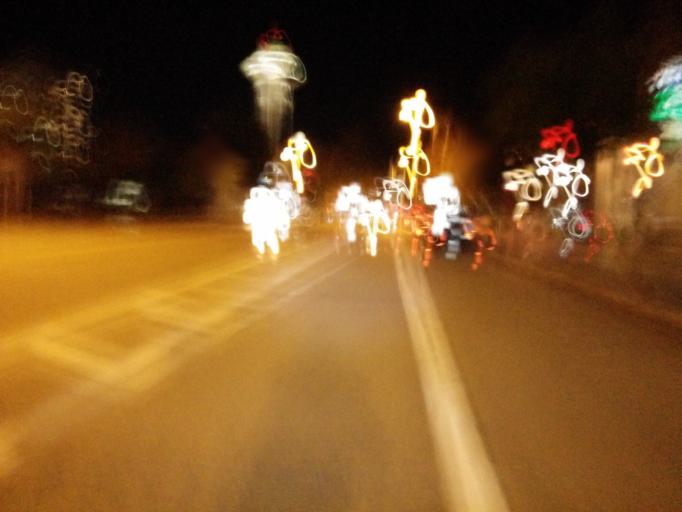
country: US
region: Washington
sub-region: King County
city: Seattle
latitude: 47.6176
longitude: -122.3416
